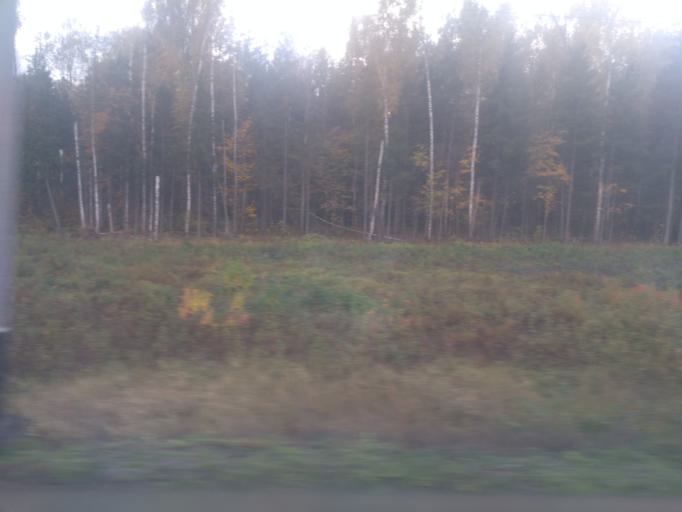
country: RU
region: Udmurtiya
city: Mozhga
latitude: 56.4336
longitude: 52.0241
